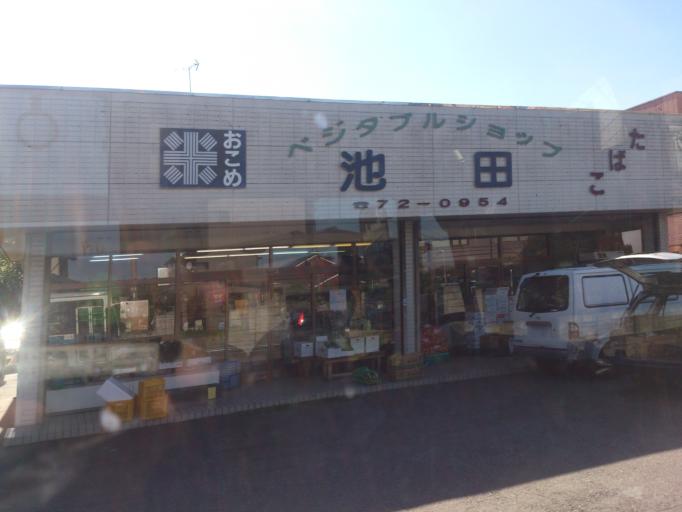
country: JP
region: Ibaraki
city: Ushiku
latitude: 35.9804
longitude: 140.1395
